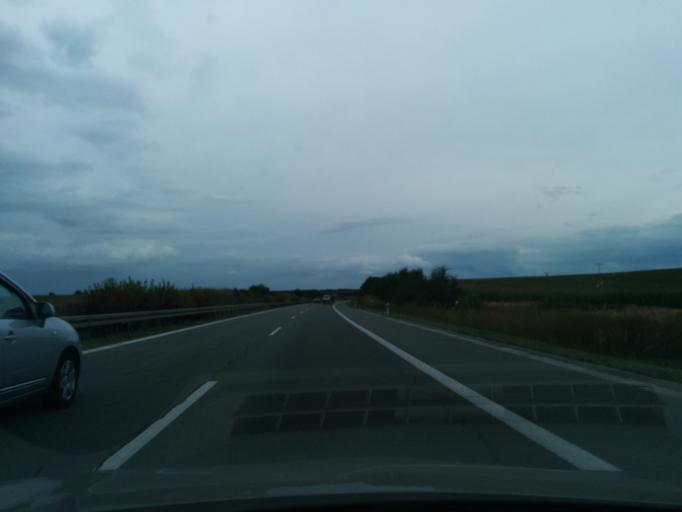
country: DE
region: Mecklenburg-Vorpommern
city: Brunn
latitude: 53.6429
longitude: 13.3699
